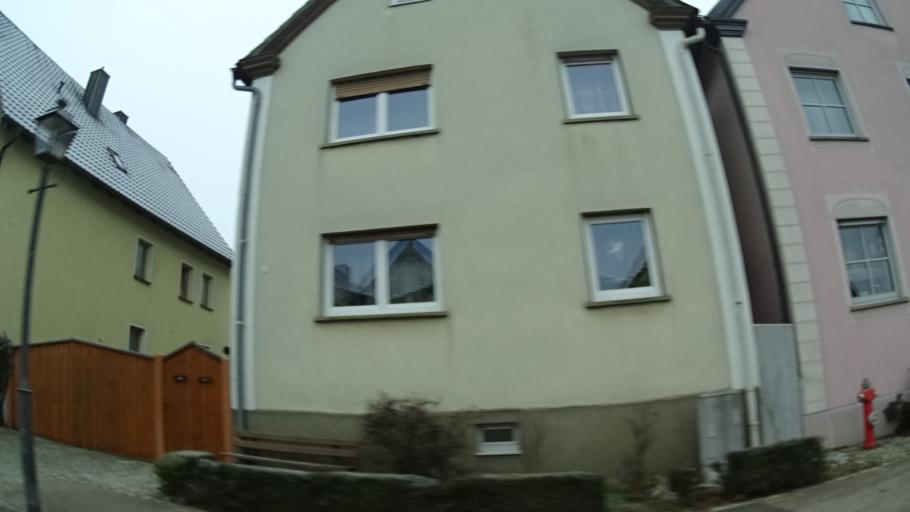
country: DE
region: Bavaria
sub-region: Regierungsbezirk Unterfranken
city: Wonfurt
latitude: 50.0135
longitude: 10.4680
